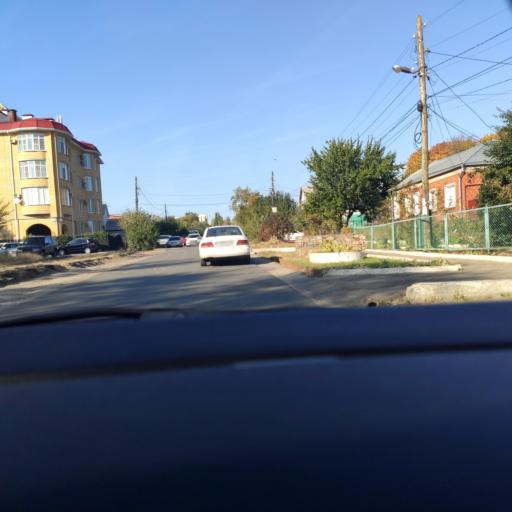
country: RU
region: Voronezj
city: Voronezh
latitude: 51.6982
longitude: 39.1688
